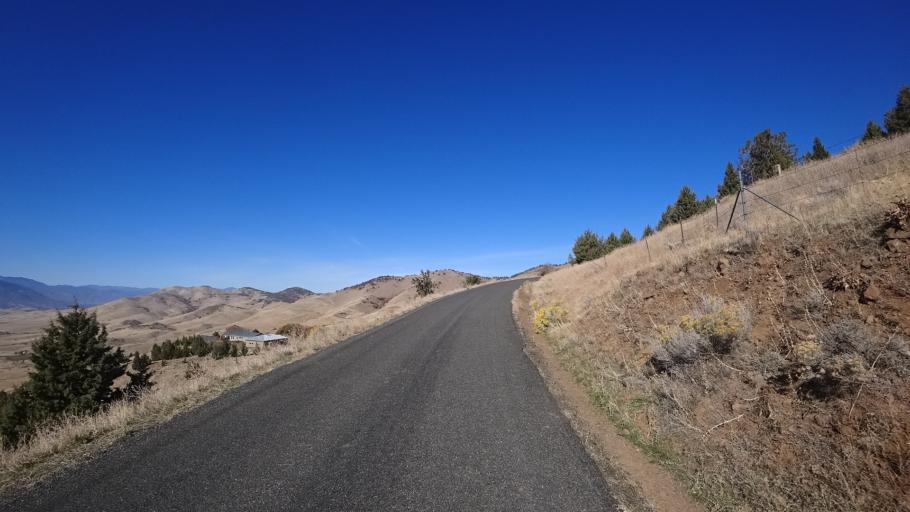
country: US
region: California
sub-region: Siskiyou County
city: Montague
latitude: 41.8255
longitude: -122.3378
